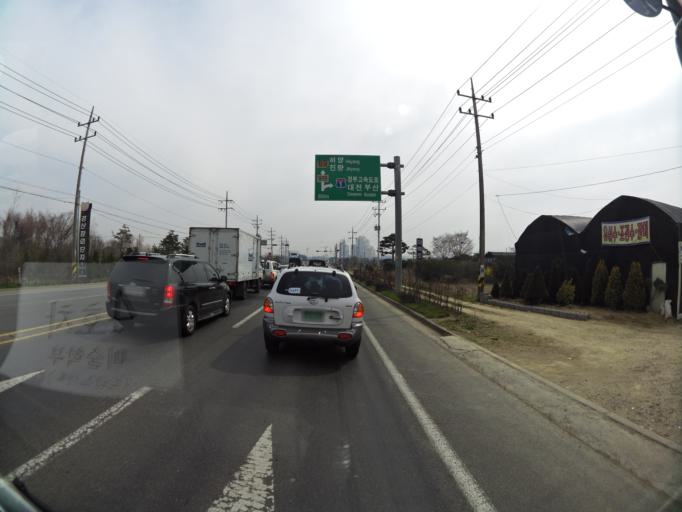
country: KR
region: Gyeongsangbuk-do
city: Hayang
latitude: 35.8734
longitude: 128.7891
